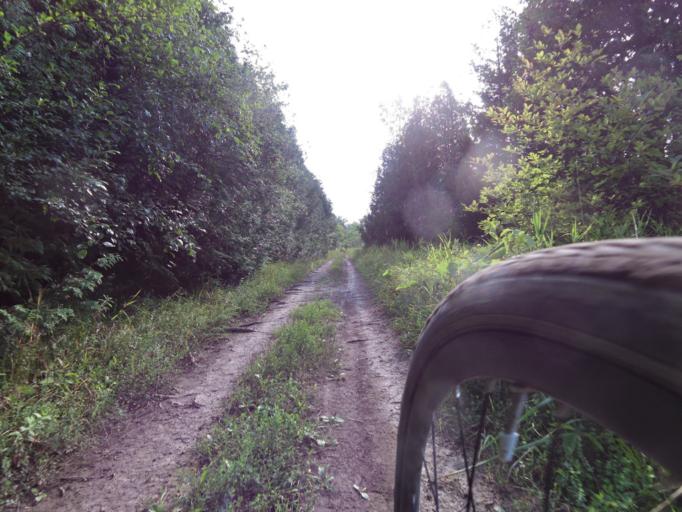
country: CA
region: Ontario
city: Quinte West
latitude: 44.0458
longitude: -77.6305
